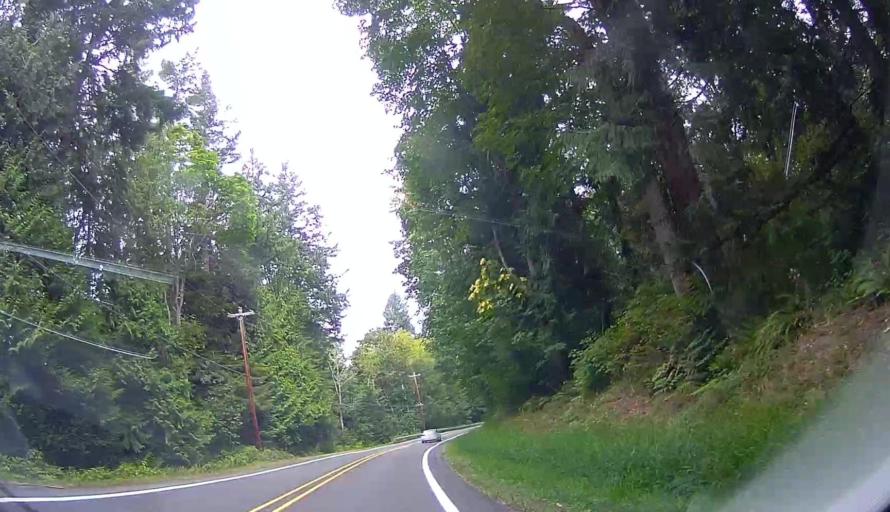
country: US
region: Washington
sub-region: Snohomish County
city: Warm Beach
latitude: 48.1357
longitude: -122.3611
